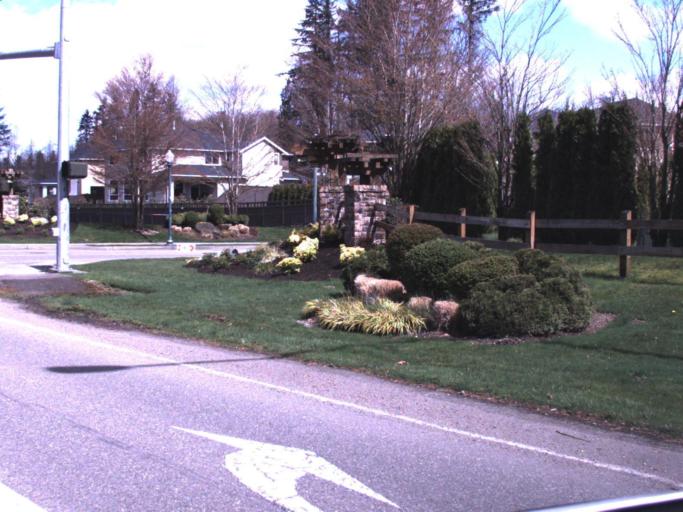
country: US
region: Washington
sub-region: King County
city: Ravensdale
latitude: 47.3541
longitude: -122.0194
